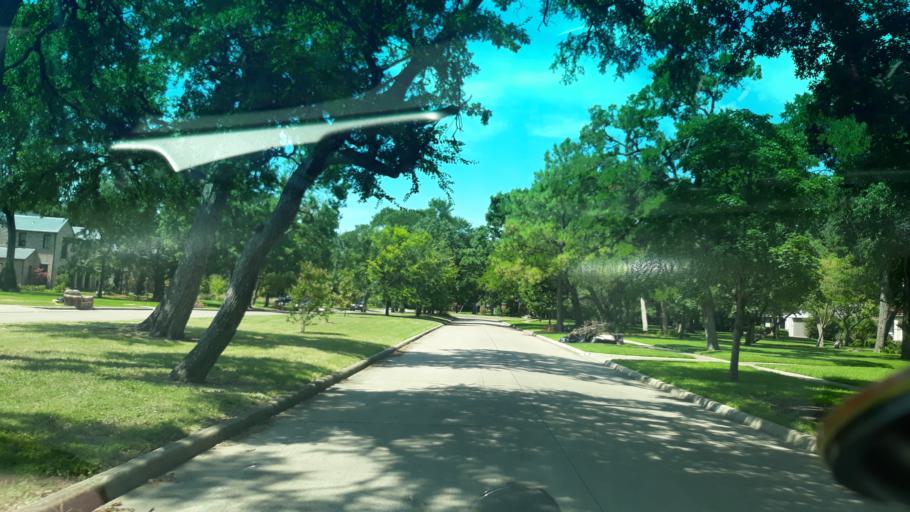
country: US
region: Texas
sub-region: Dallas County
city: Highland Park
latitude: 32.8127
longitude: -96.7195
